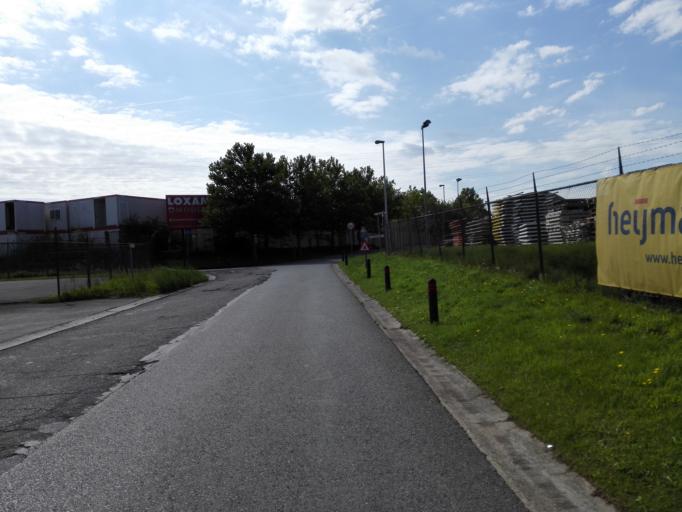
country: BE
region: Flanders
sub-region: Provincie Antwerpen
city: Aartselaar
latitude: 51.1231
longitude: 4.3693
